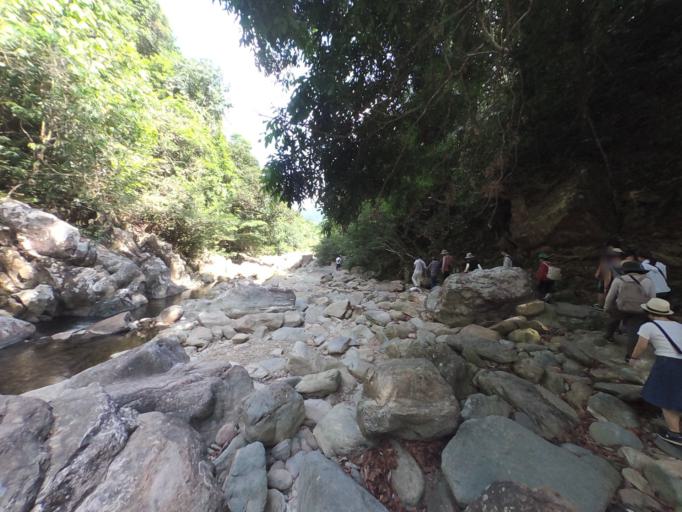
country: VN
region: Thua Thien-Hue
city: A Luoi
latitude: 16.3062
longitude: 107.3242
